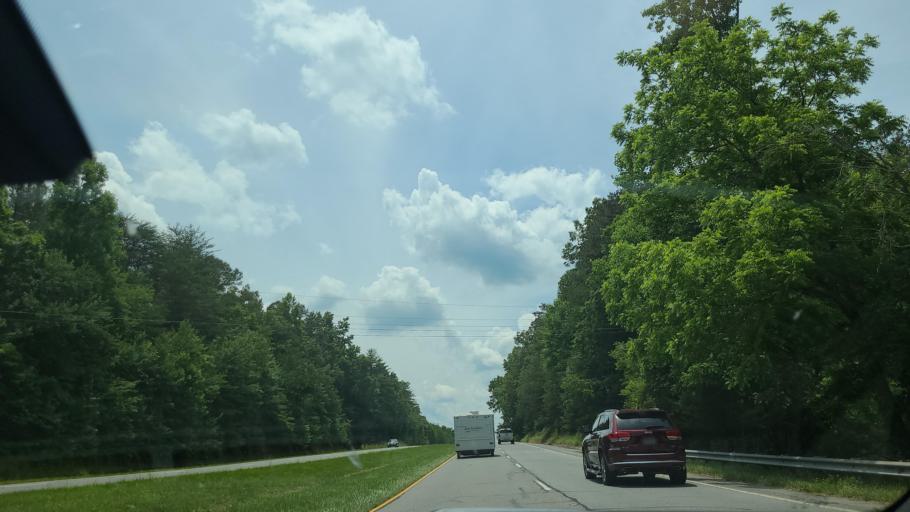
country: US
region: North Carolina
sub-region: Cherokee County
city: Murphy
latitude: 35.0219
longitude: -84.1731
